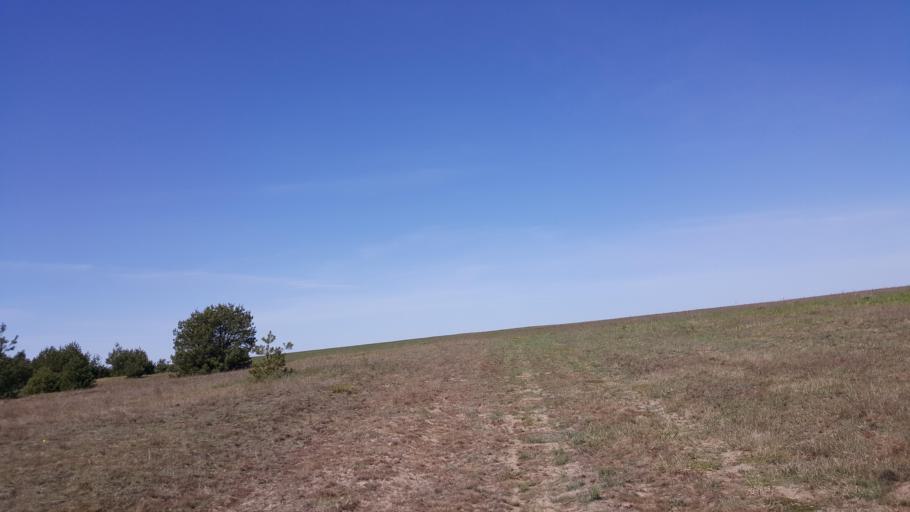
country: BY
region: Brest
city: Kamyanyets
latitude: 52.4461
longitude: 23.9013
